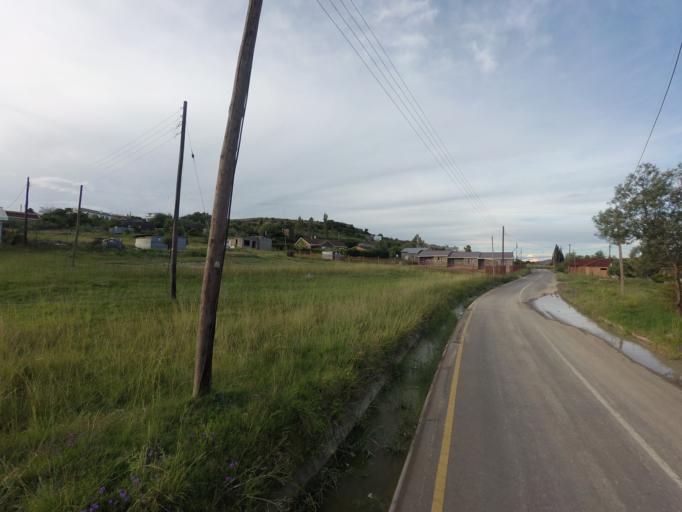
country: LS
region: Maseru
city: Maseru
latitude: -29.3081
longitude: 27.5060
